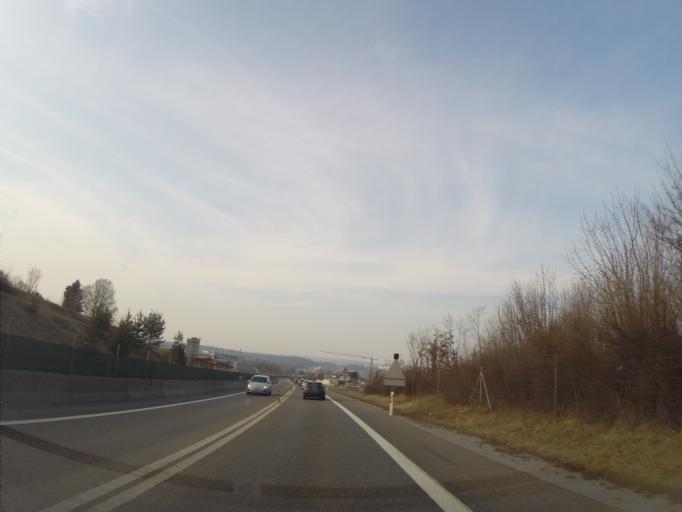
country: CH
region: Zurich
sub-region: Bezirk Andelfingen
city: Kleinandelfingen
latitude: 47.5913
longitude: 8.6906
